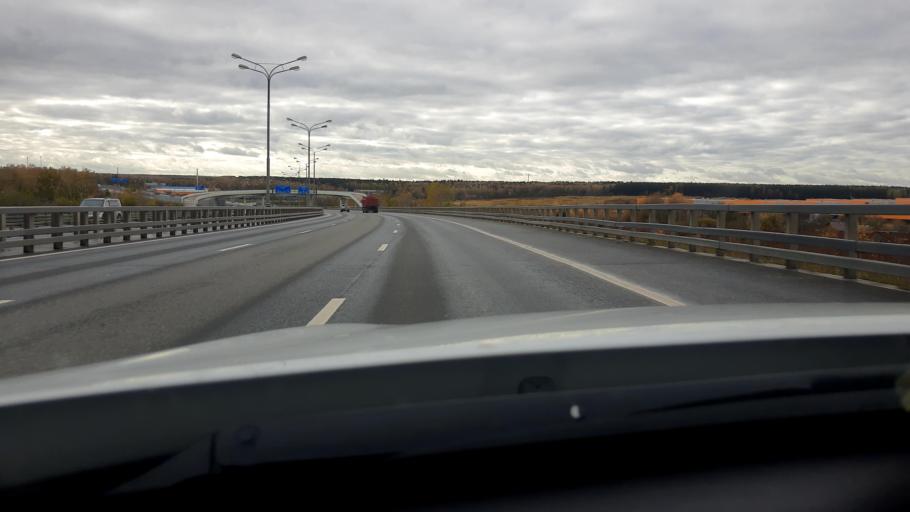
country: RU
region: Moscow
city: Vnukovo
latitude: 55.5826
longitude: 37.2094
